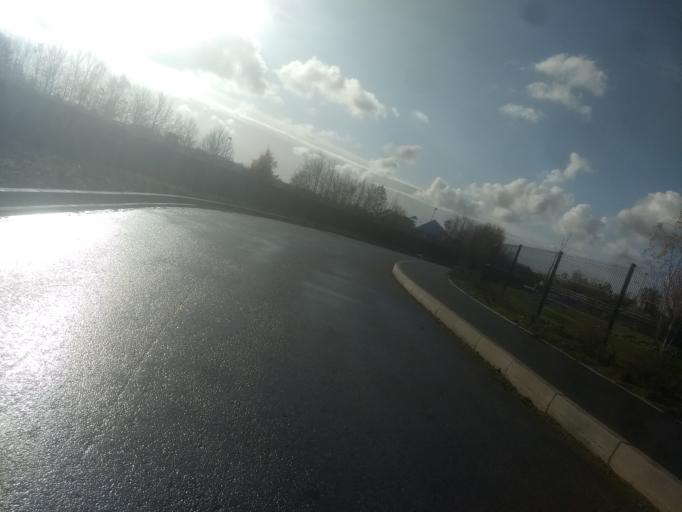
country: FR
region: Nord-Pas-de-Calais
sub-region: Departement du Pas-de-Calais
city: Anzin-Saint-Aubin
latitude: 50.3056
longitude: 2.7338
